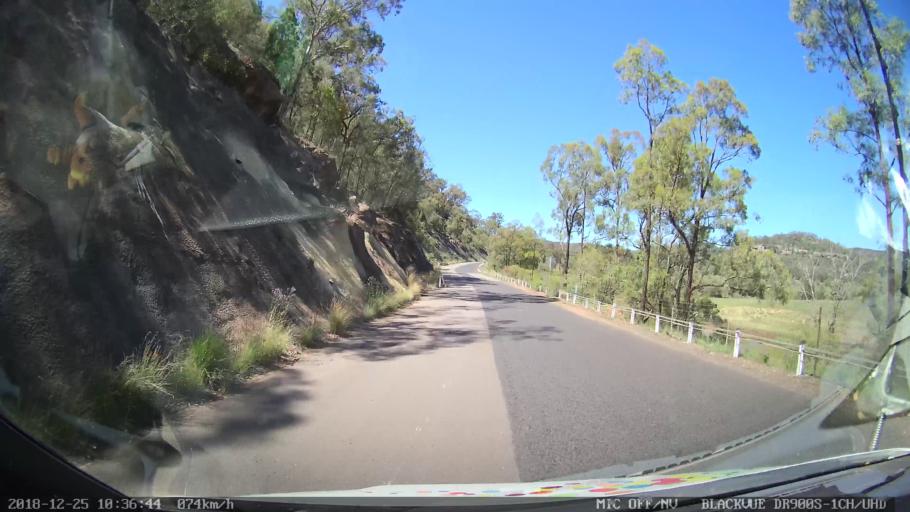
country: AU
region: New South Wales
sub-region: Upper Hunter Shire
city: Merriwa
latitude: -32.4069
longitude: 150.3835
